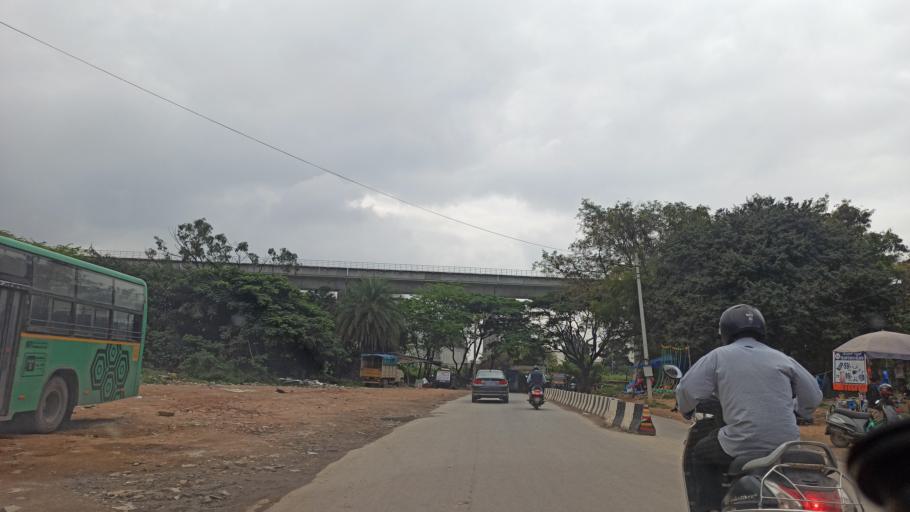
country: IN
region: Karnataka
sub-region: Bangalore Urban
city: Bangalore
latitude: 13.0016
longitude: 77.6834
